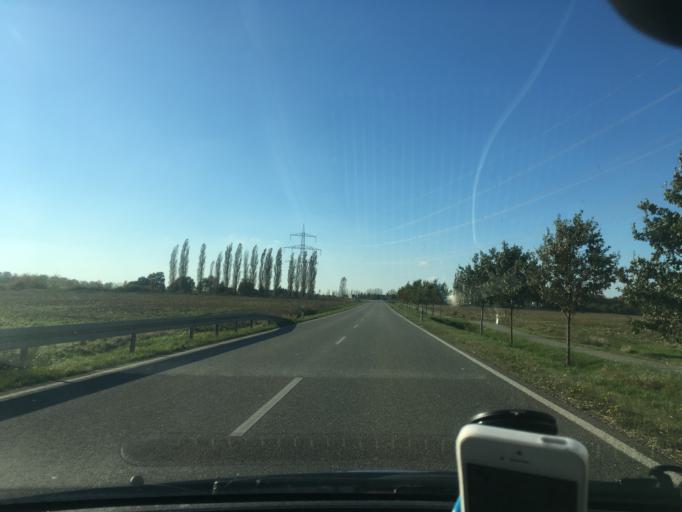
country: DE
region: Mecklenburg-Vorpommern
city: Wittenburg
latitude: 53.5211
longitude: 11.0608
